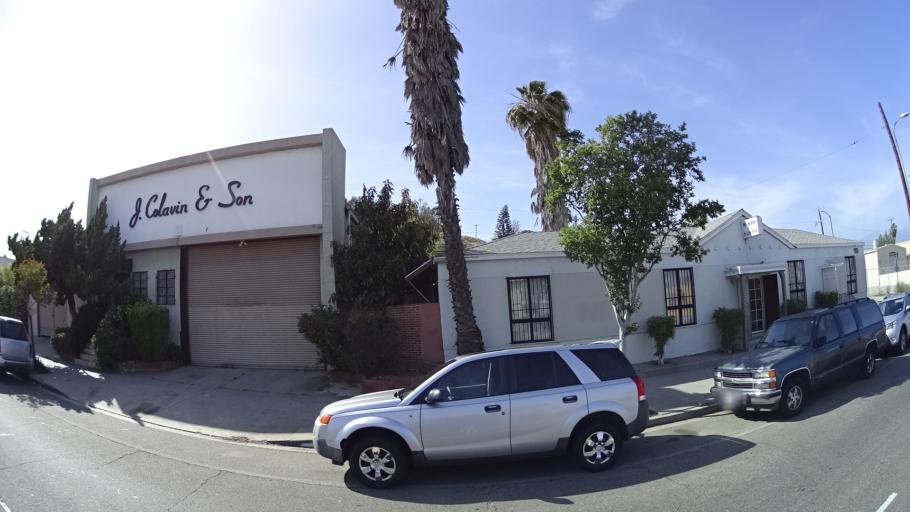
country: US
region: California
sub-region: Los Angeles County
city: Belvedere
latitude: 34.0758
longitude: -118.1698
